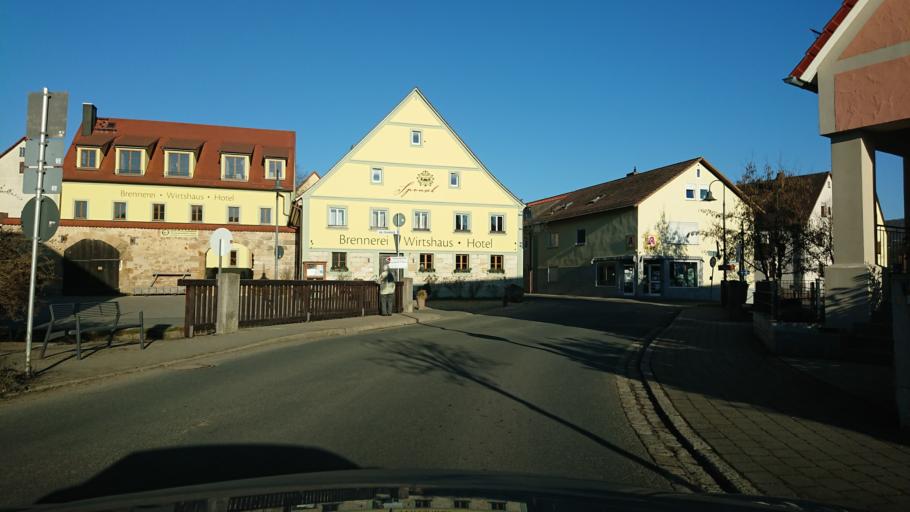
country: DE
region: Bavaria
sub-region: Upper Franconia
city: Kirchehrenbach
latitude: 49.7342
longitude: 11.1467
